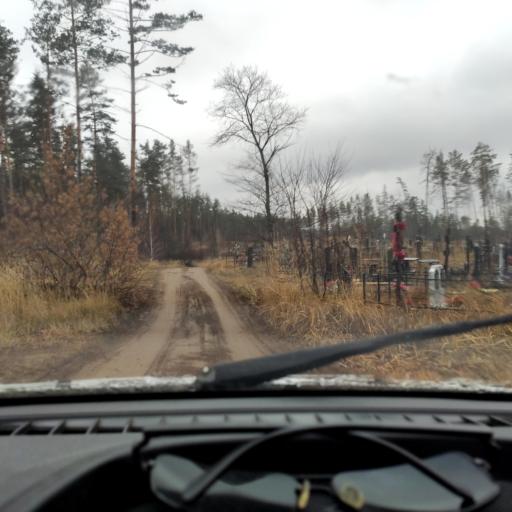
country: RU
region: Samara
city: Zhigulevsk
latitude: 53.5379
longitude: 49.5546
